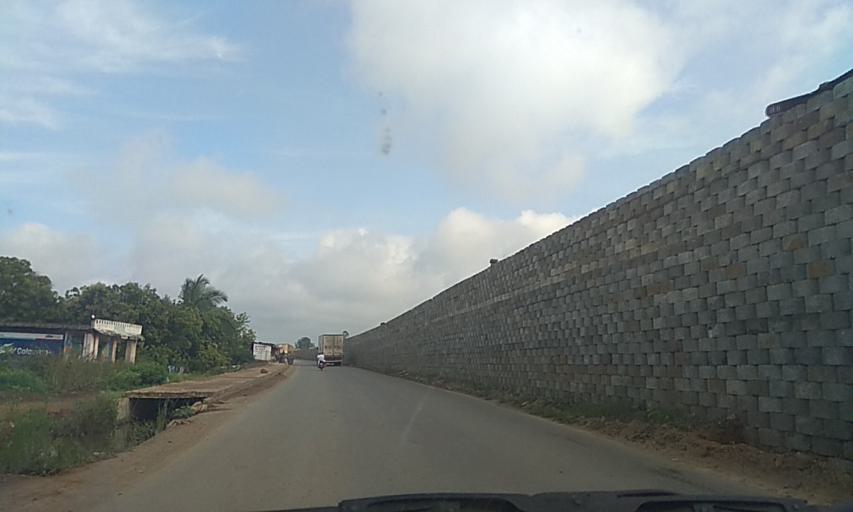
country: IN
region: Karnataka
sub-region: Haveri
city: Savanur
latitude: 14.8709
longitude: 75.3186
